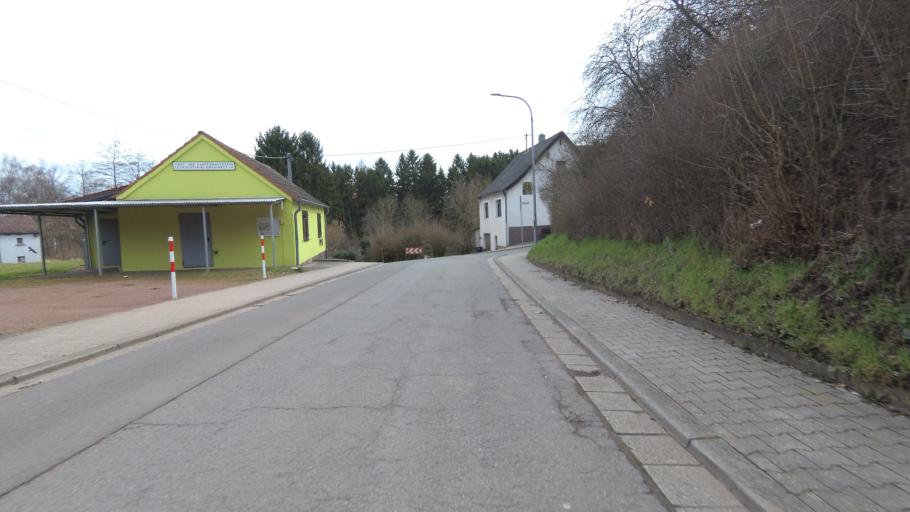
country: DE
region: Saarland
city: Schiffweiler
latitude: 49.3689
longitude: 7.1133
